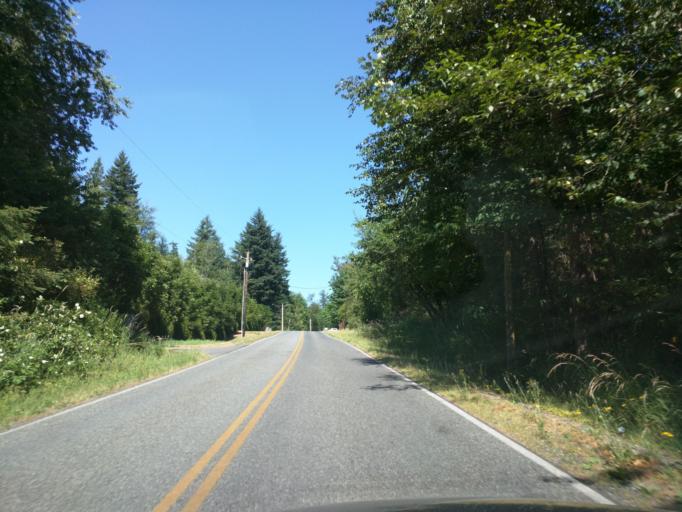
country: US
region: Washington
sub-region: Whatcom County
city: Nooksack
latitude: 48.9205
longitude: -122.2736
